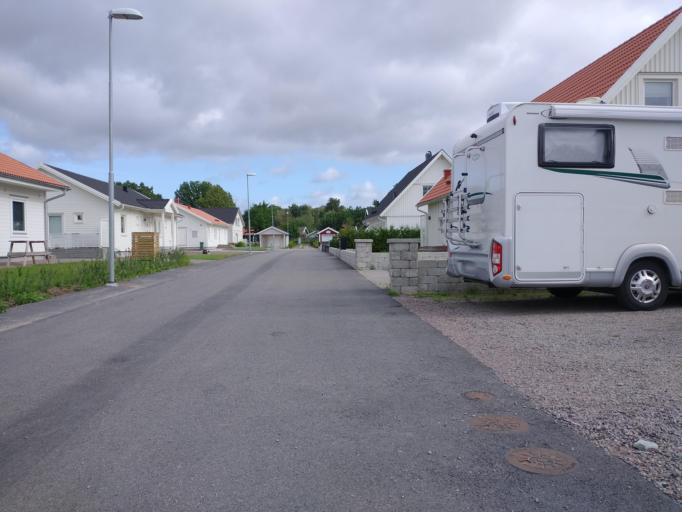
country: SE
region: Kalmar
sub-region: Kalmar Kommun
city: Lindsdal
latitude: 56.7787
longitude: 16.3017
